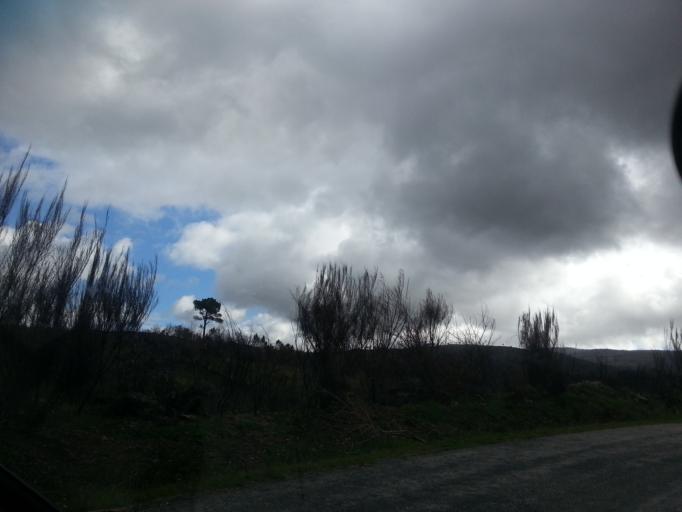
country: PT
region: Guarda
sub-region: Fornos de Algodres
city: Fornos de Algodres
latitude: 40.5684
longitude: -7.4669
